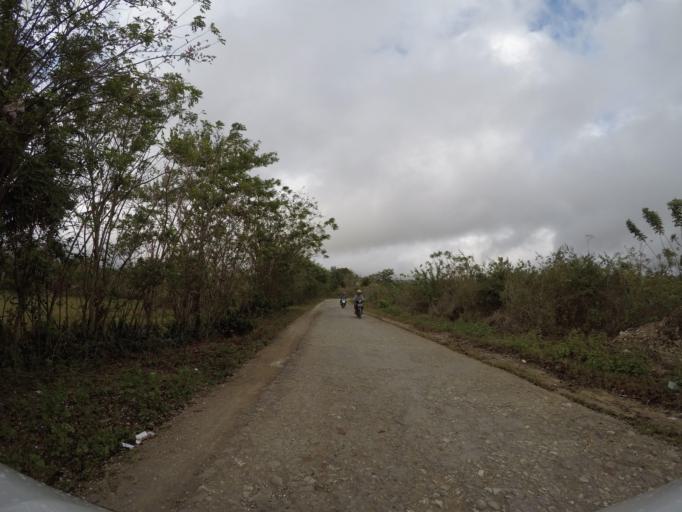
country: TL
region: Lautem
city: Lospalos
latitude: -8.5292
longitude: 126.9857
